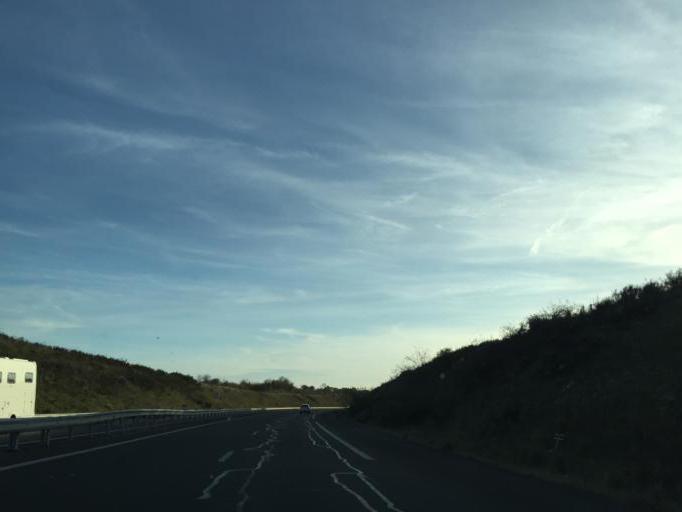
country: FR
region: Rhone-Alpes
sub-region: Departement de l'Isere
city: Satolas-et-Bonce
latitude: 45.7077
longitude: 5.0995
